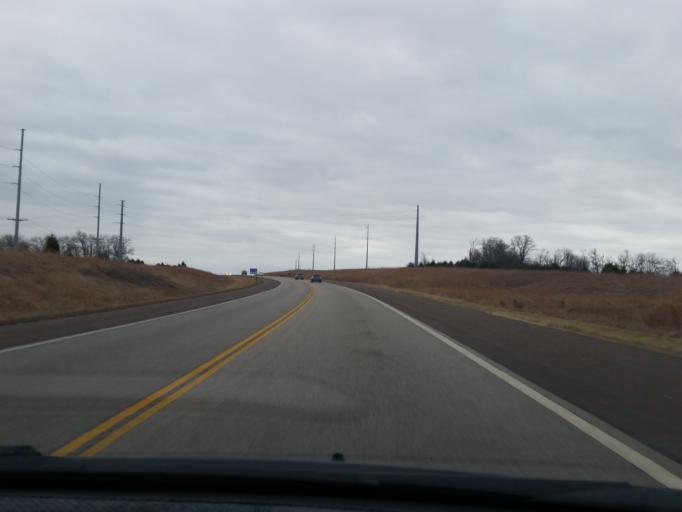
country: US
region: Kansas
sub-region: Douglas County
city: Lawrence
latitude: 38.9885
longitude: -95.3424
